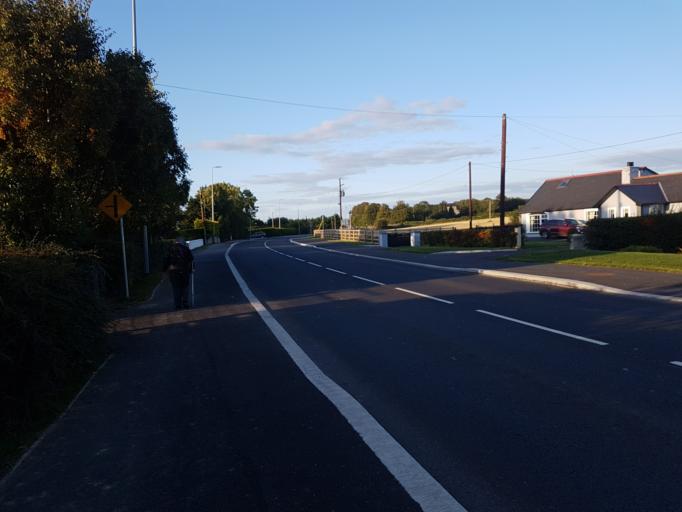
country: IE
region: Leinster
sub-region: Kilkenny
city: Kilkenny
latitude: 52.6326
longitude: -7.2757
